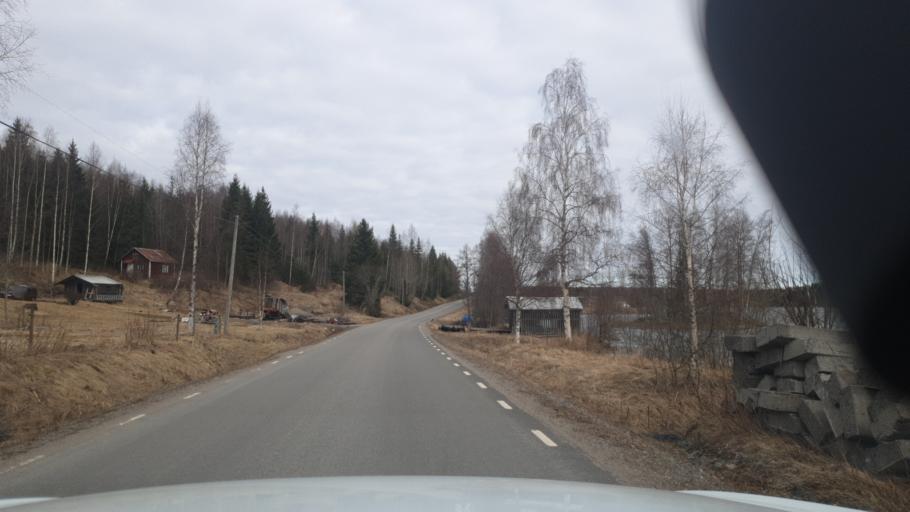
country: SE
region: Vaermland
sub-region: Eda Kommun
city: Charlottenberg
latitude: 59.9427
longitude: 12.5231
